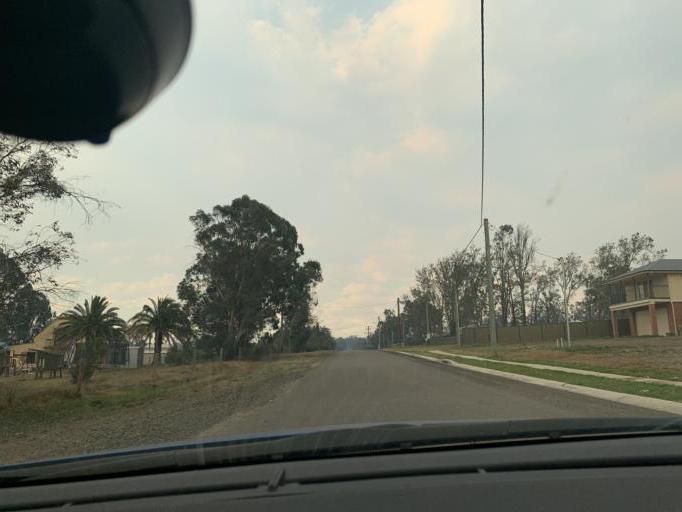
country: AU
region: New South Wales
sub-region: Cessnock
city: Cessnock
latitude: -32.9236
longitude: 151.3100
